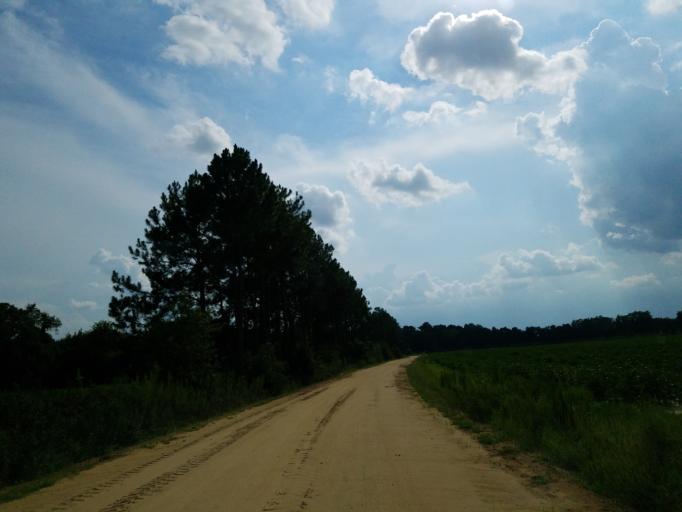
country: US
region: Georgia
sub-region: Dooly County
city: Unadilla
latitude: 32.1850
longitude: -83.7456
